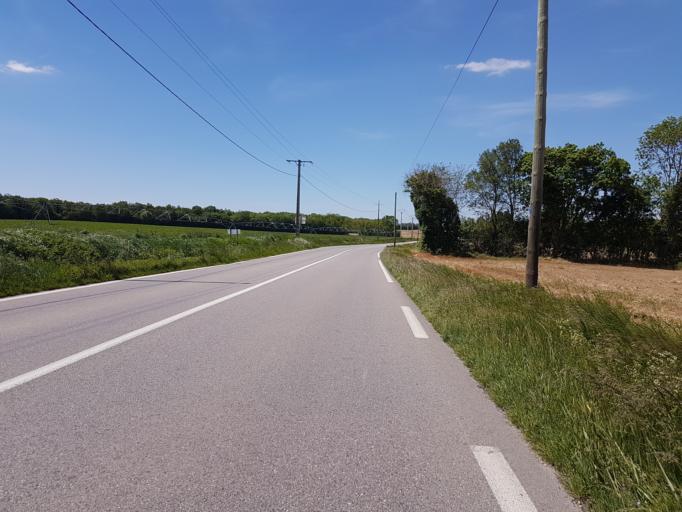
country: FR
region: Rhone-Alpes
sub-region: Departement de l'Isere
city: Chavanoz
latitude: 45.7847
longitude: 5.1502
